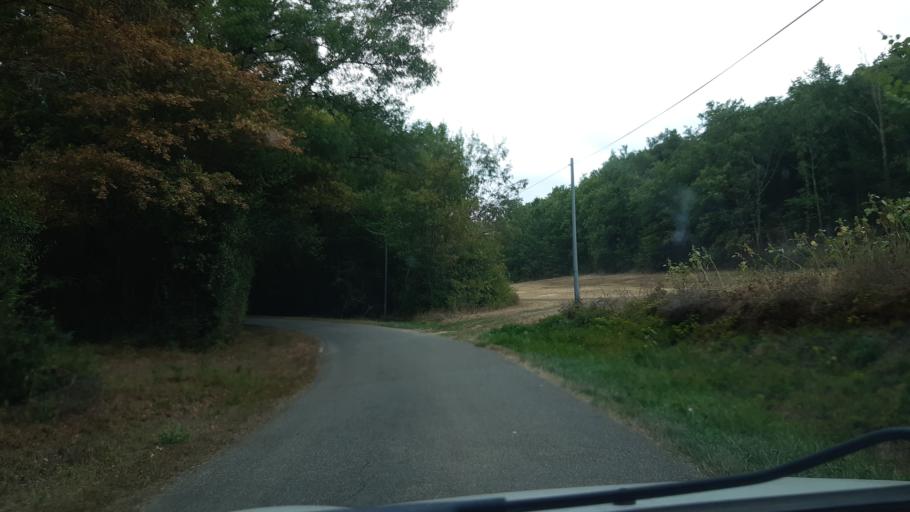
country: FR
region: Midi-Pyrenees
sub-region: Departement du Gers
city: Gimont
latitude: 43.6984
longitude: 0.9795
